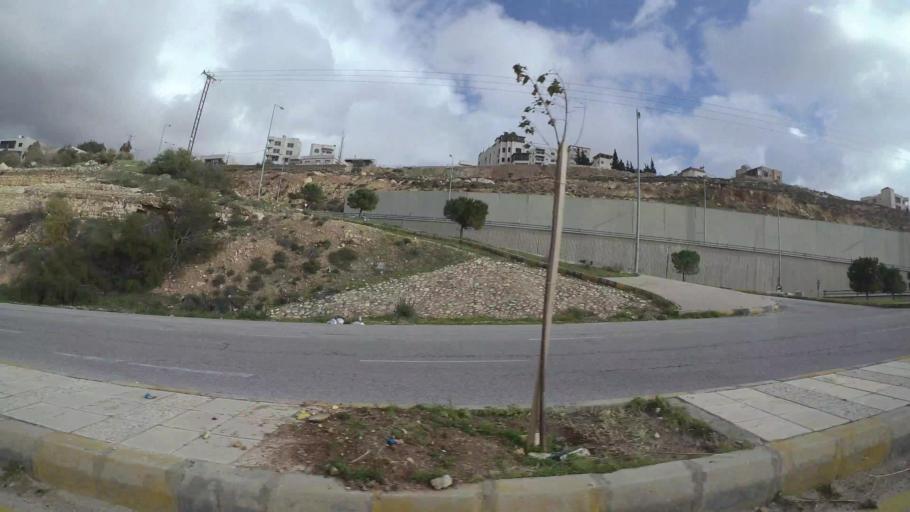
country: JO
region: Amman
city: Al Jubayhah
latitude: 32.0723
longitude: 35.8769
